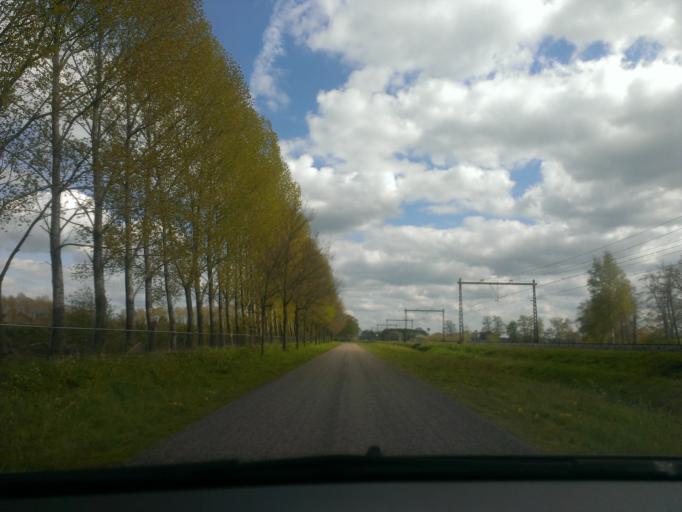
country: NL
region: Overijssel
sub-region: Gemeente Almelo
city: Almelo
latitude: 52.3239
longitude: 6.7017
